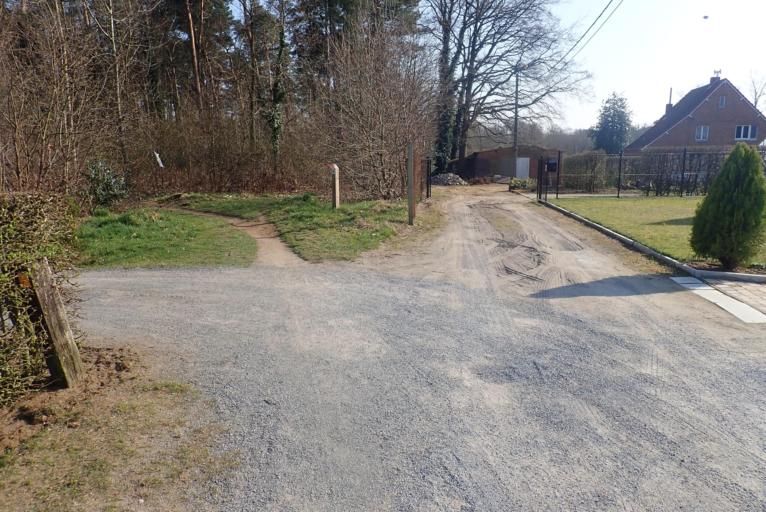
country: BE
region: Flanders
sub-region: Provincie Vlaams-Brabant
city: Aarschot
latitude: 51.0042
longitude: 4.8600
